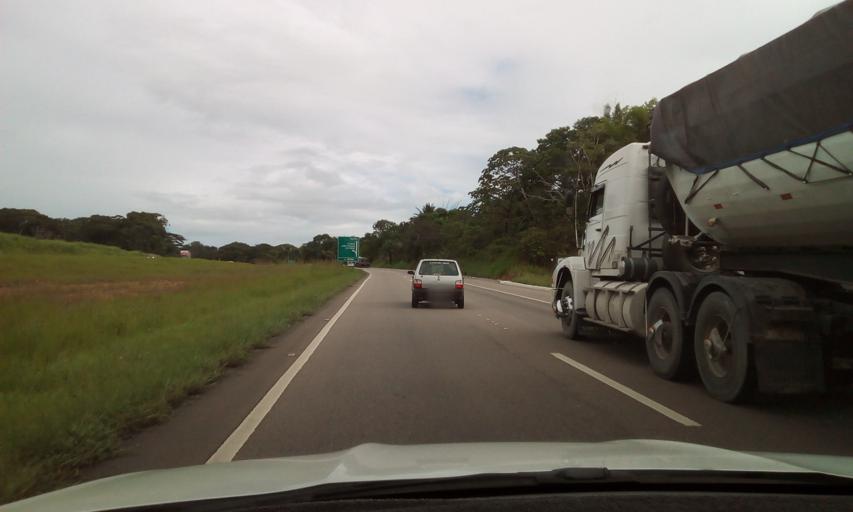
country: BR
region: Pernambuco
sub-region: Goiana
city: Goiana
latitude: -7.5897
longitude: -34.9870
